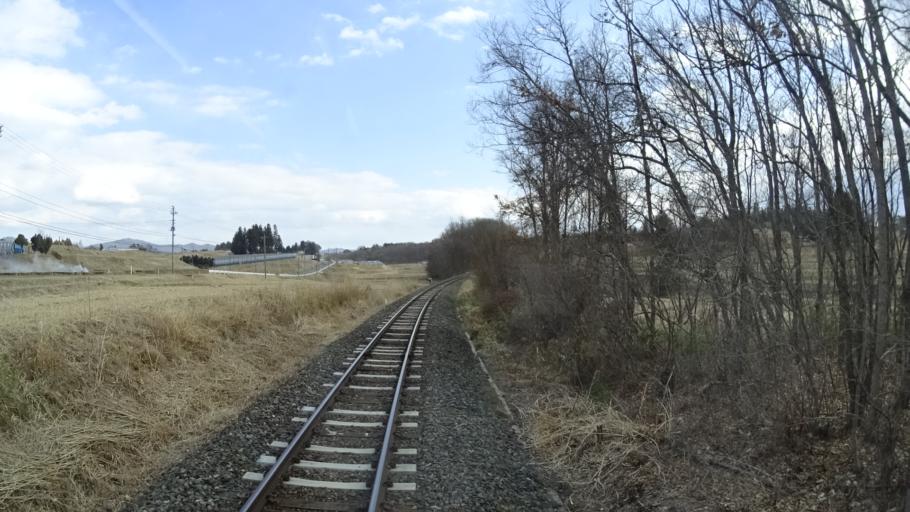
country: JP
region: Iwate
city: Hanamaki
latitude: 39.3977
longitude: 141.2105
